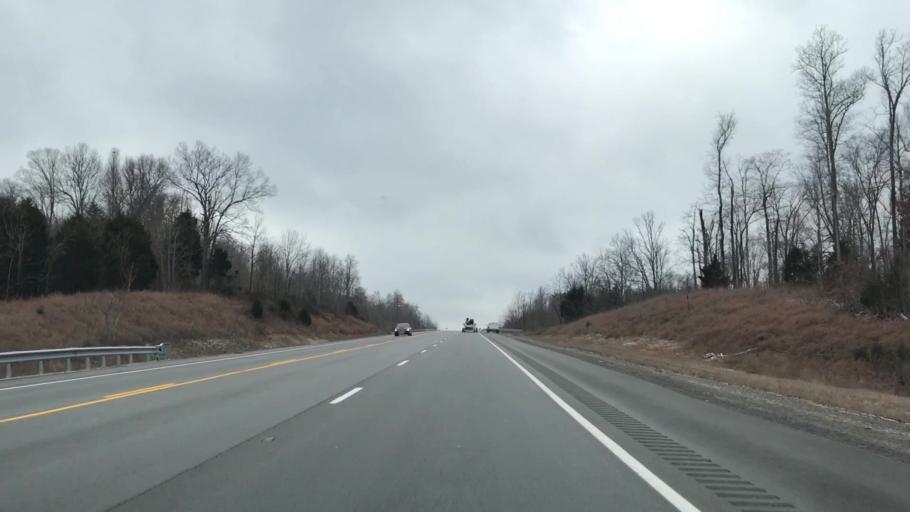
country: US
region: Kentucky
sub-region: Adair County
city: Columbia
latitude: 37.0291
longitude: -85.3849
